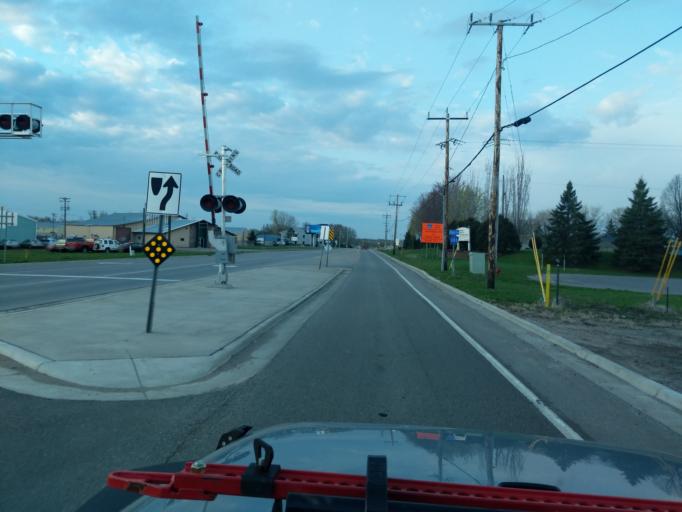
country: US
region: Minnesota
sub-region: Hennepin County
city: Rogers
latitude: 45.1693
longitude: -93.5216
